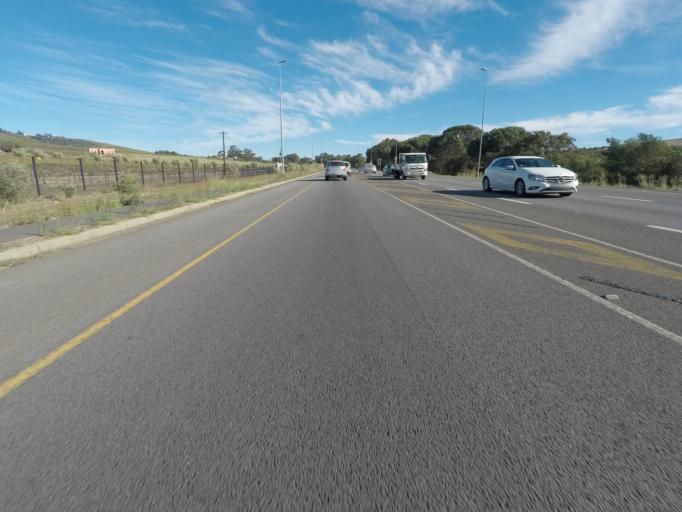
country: ZA
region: Western Cape
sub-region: Cape Winelands District Municipality
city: Stellenbosch
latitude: -33.9012
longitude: 18.8393
